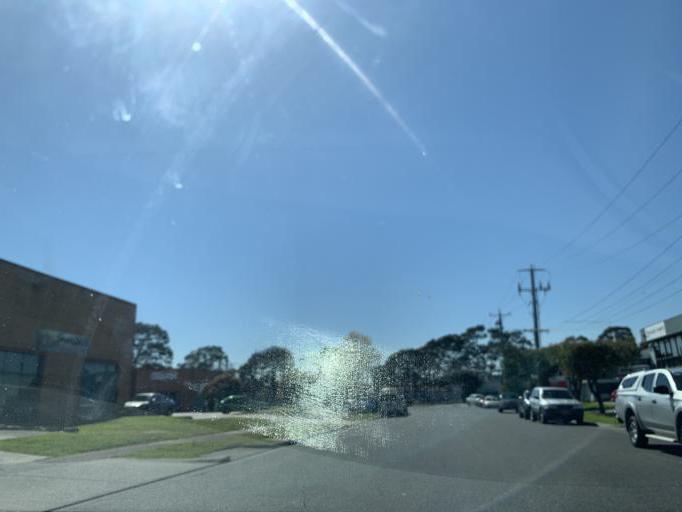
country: AU
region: Victoria
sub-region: Greater Dandenong
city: Dandenong
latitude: -37.9875
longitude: 145.2031
